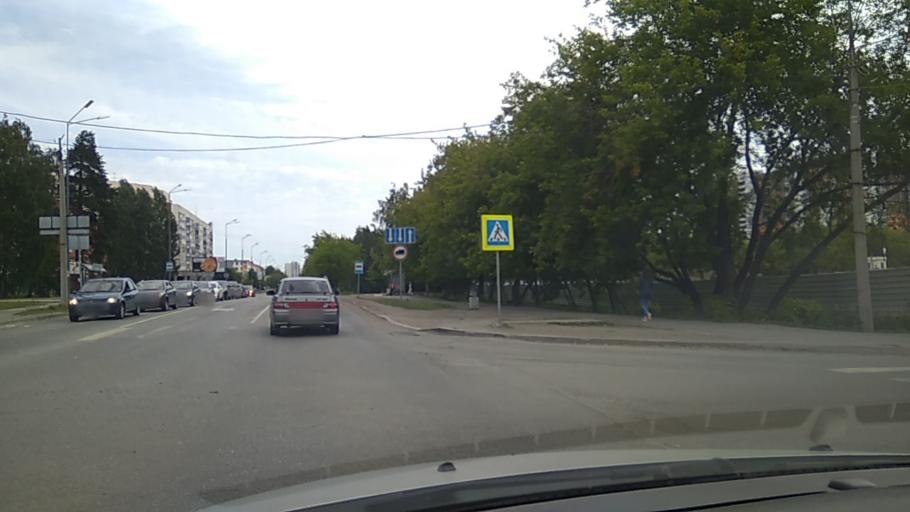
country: RU
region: Sverdlovsk
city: Verkhnyaya Pyshma
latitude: 56.9798
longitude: 60.5521
